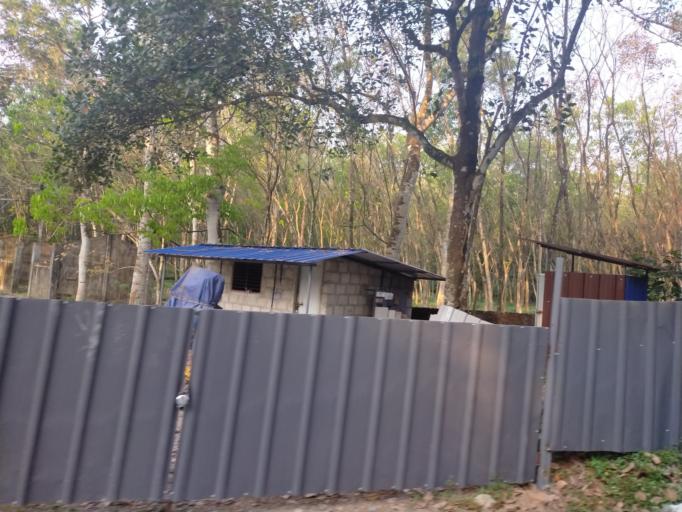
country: IN
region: Kerala
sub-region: Kottayam
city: Vaikam
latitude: 9.7489
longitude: 76.5083
